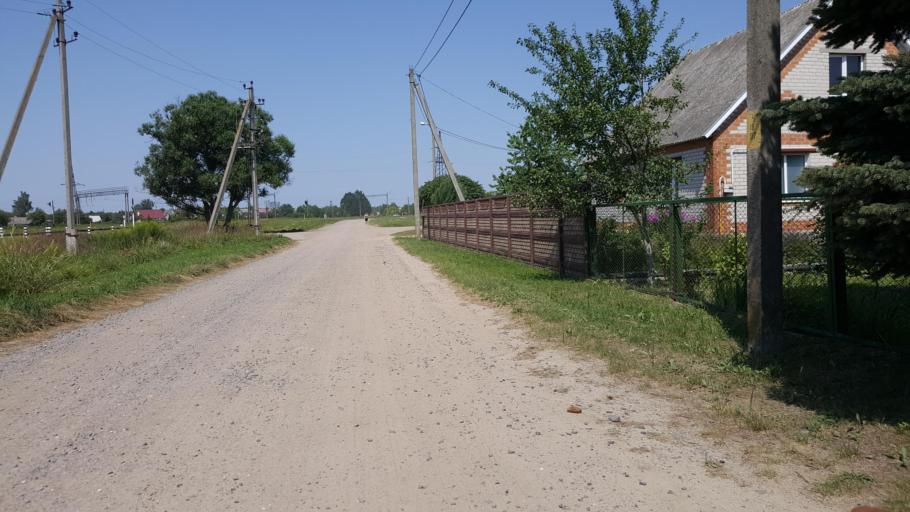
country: BY
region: Brest
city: Zhabinka
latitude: 52.1938
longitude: 24.0058
